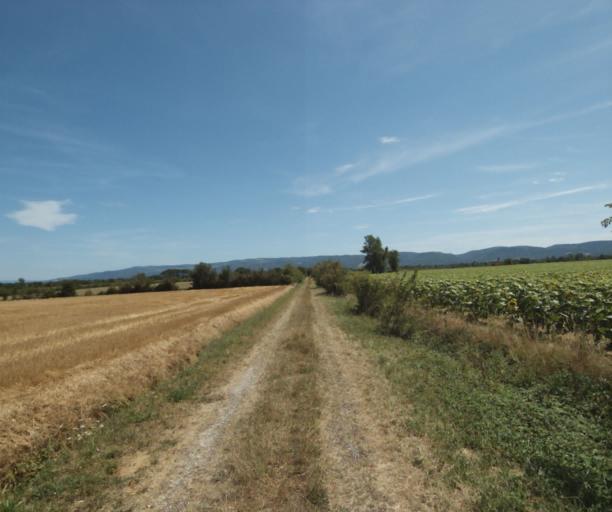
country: FR
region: Midi-Pyrenees
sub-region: Departement de la Haute-Garonne
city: Revel
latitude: 43.5009
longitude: 2.0125
